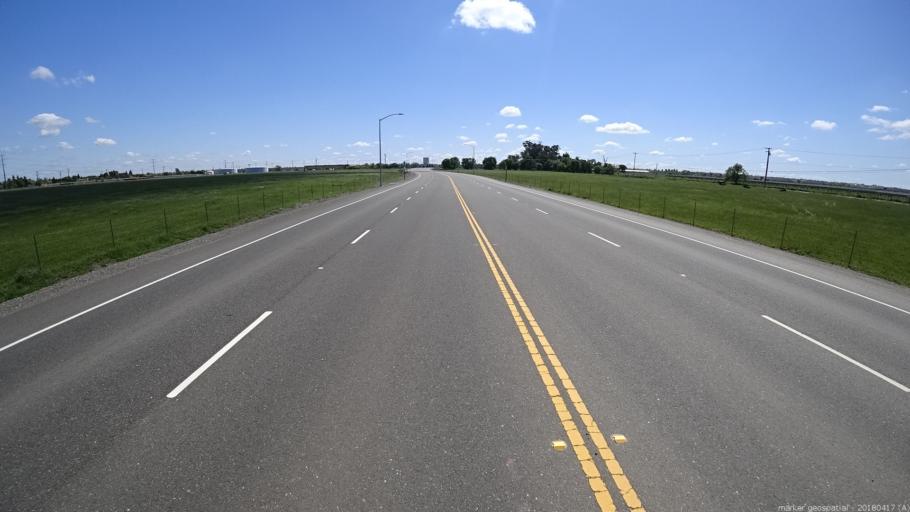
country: US
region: California
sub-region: Sacramento County
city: Laguna
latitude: 38.4372
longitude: -121.4629
